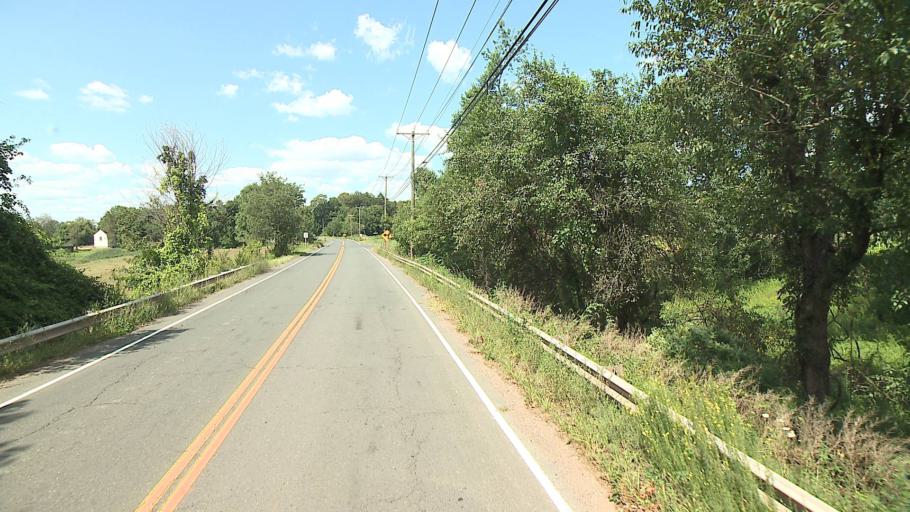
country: US
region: Connecticut
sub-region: Hartford County
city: Broad Brook
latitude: 41.9356
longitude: -72.5120
